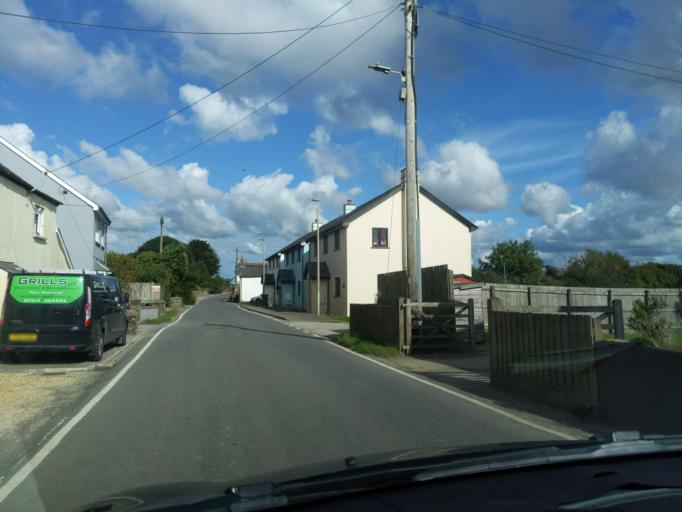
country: GB
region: England
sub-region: Devon
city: Great Torrington
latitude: 50.9187
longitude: -4.2106
